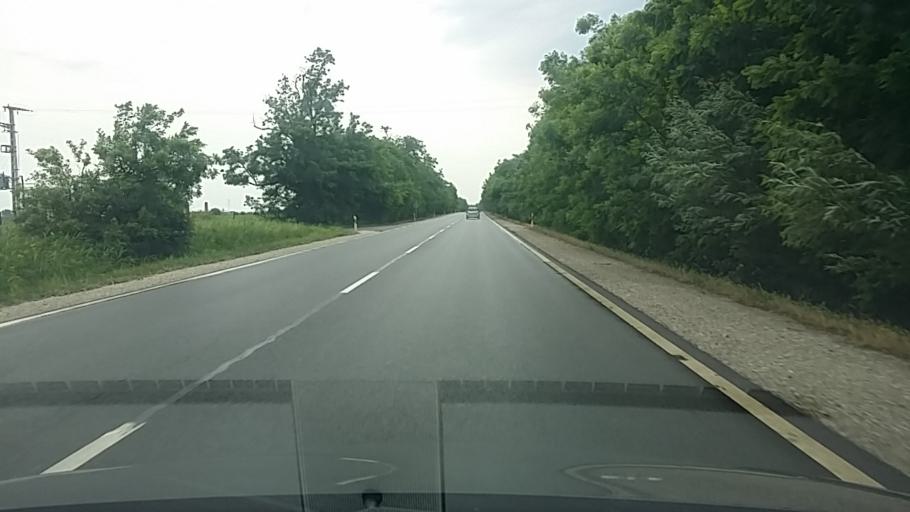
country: HU
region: Hajdu-Bihar
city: Teglas
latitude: 47.7513
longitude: 21.6773
